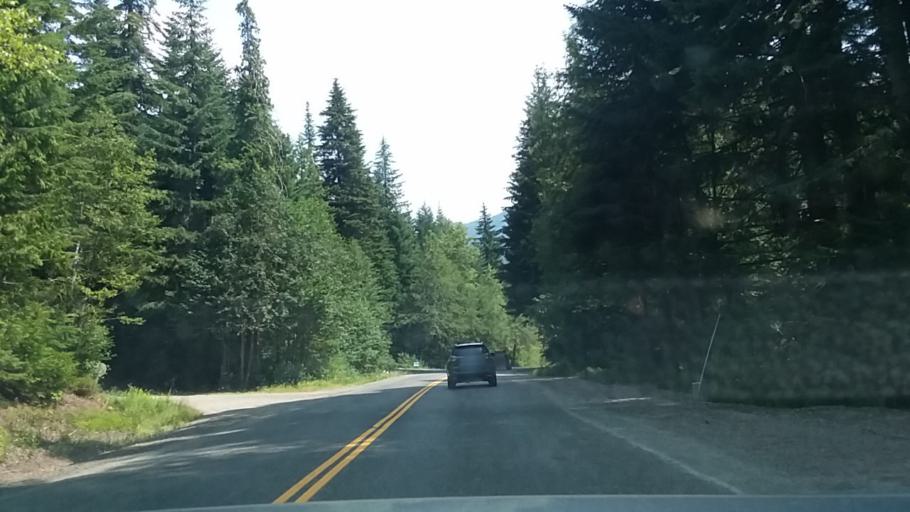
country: US
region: Washington
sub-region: Kittitas County
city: Cle Elum
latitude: 47.3309
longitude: -121.2624
